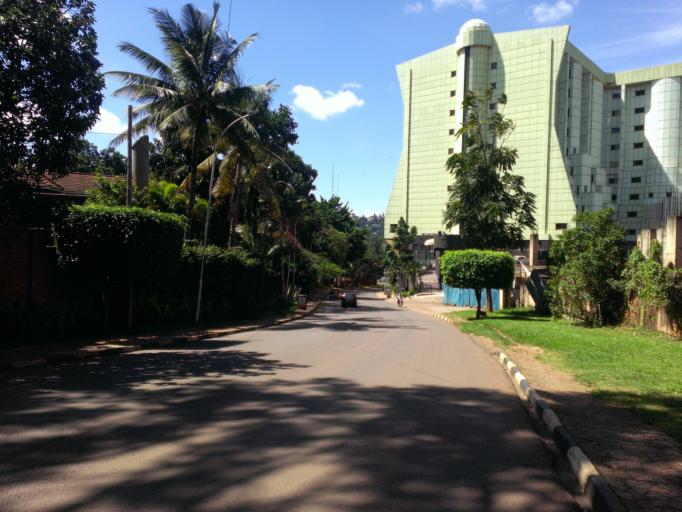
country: UG
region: Central Region
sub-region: Kampala District
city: Kampala
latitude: 0.3181
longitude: 32.5845
